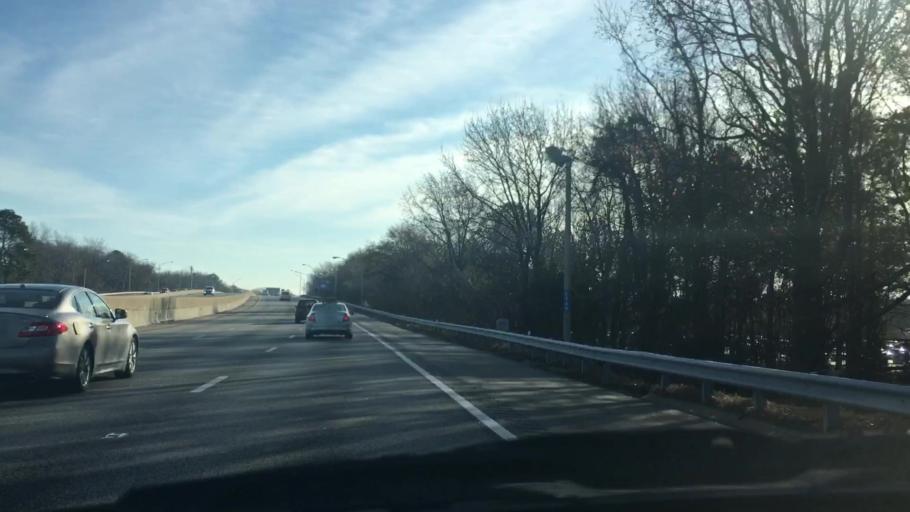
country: US
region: Virginia
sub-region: City of Norfolk
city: Norfolk
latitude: 36.8810
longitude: -76.2117
